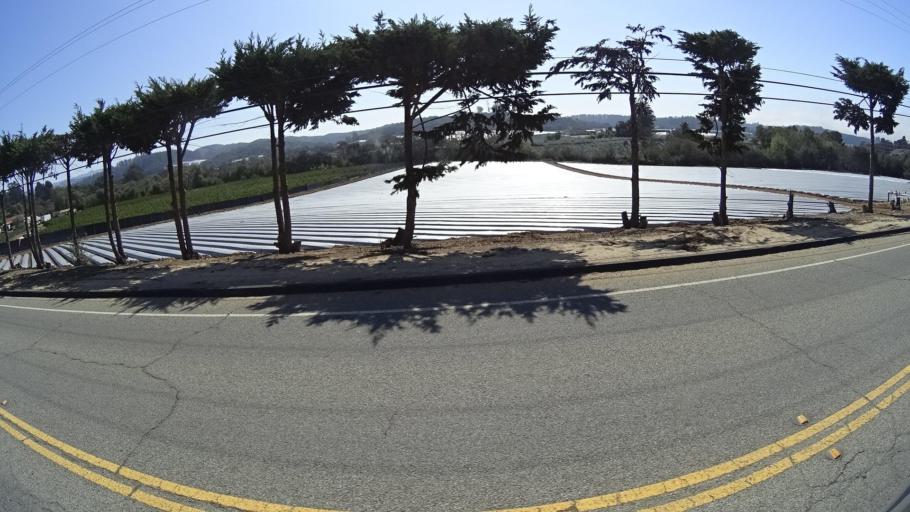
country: US
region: California
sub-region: San Benito County
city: Aromas
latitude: 36.8688
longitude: -121.6734
